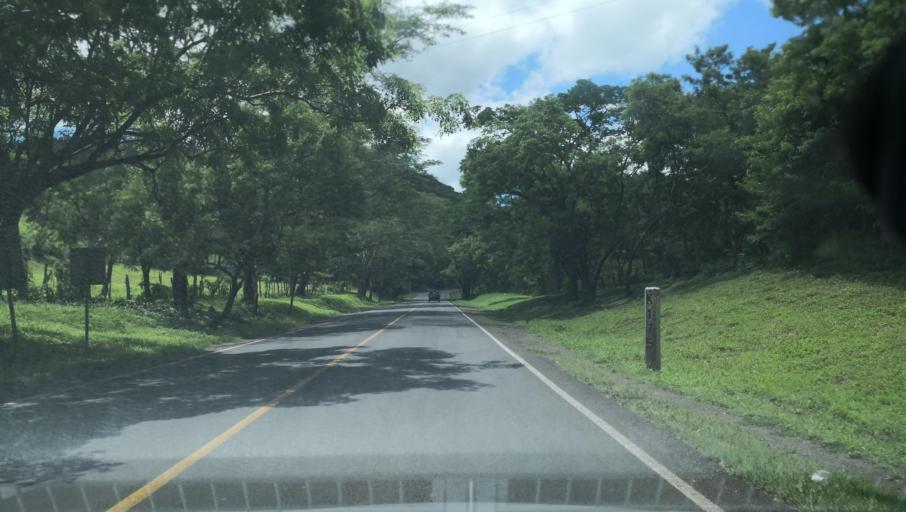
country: NI
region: Esteli
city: Condega
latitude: 13.3022
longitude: -86.3502
